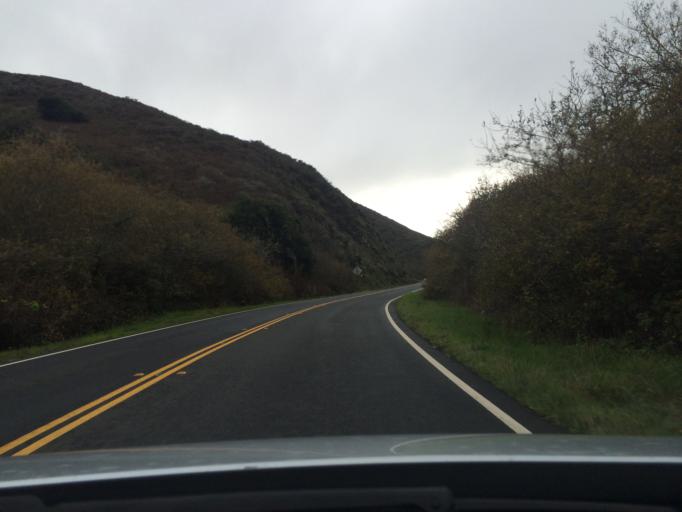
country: US
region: California
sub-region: Marin County
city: Inverness
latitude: 38.2245
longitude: -122.9165
